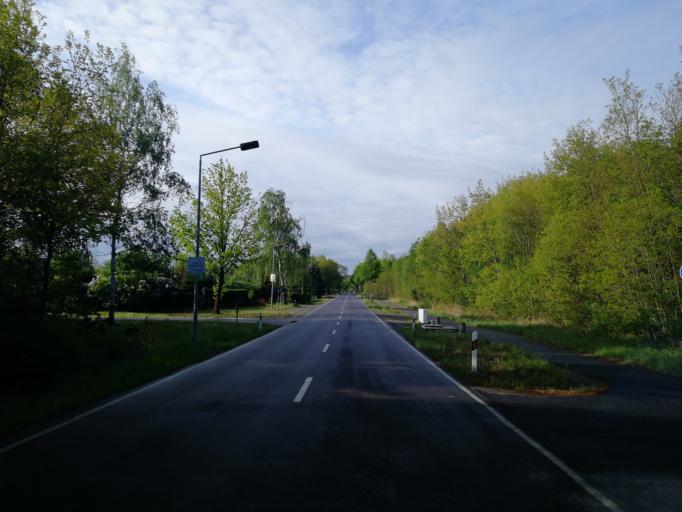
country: DE
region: Brandenburg
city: Lauchhammer
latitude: 51.5135
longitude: 13.7490
